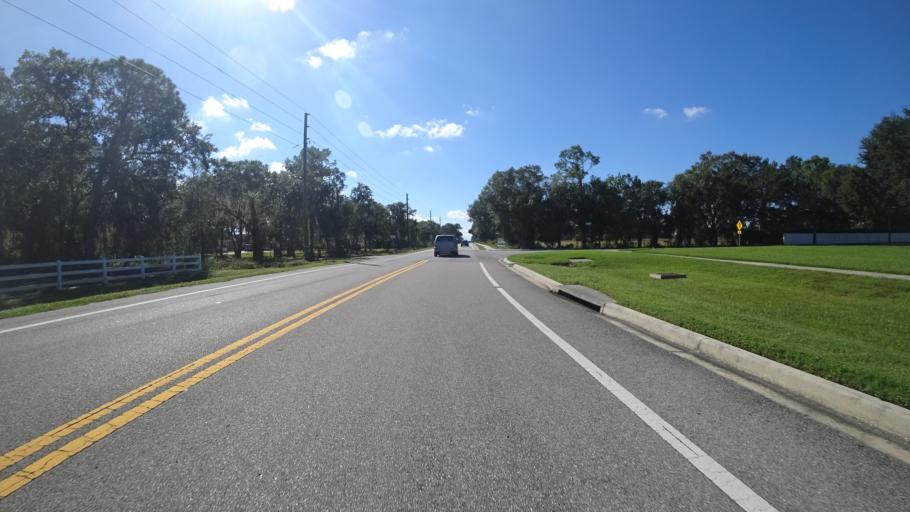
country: US
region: Florida
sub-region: Manatee County
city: Ellenton
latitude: 27.5654
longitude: -82.4254
